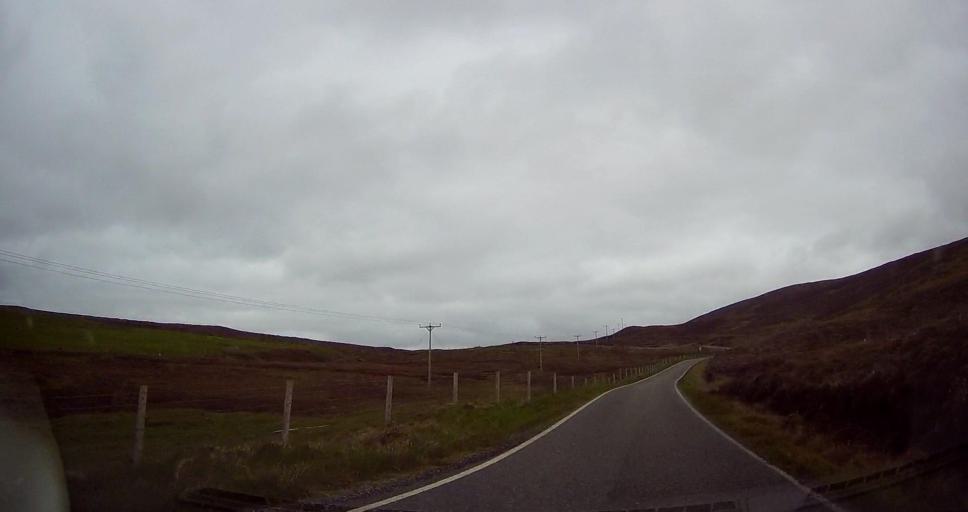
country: GB
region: Scotland
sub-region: Shetland Islands
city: Lerwick
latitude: 60.3076
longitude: -1.3380
